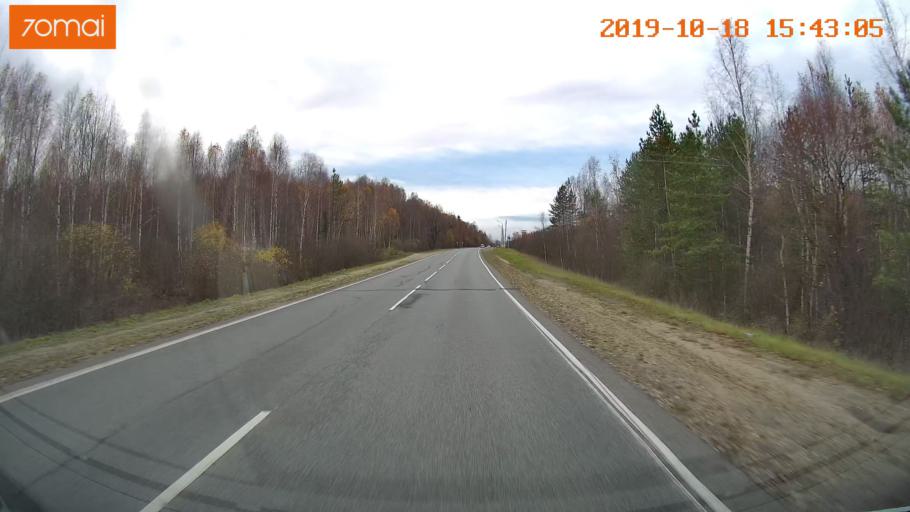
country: RU
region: Vladimir
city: Golovino
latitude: 55.9629
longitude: 40.5565
